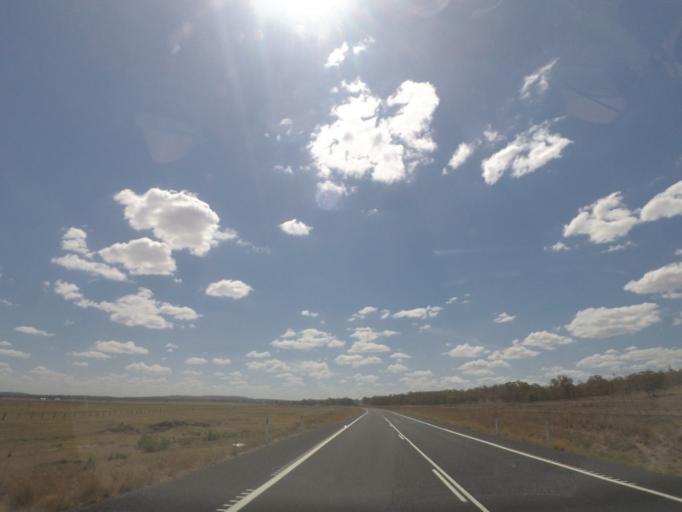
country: AU
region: Queensland
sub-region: Southern Downs
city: Warwick
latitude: -28.1803
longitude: 151.7873
